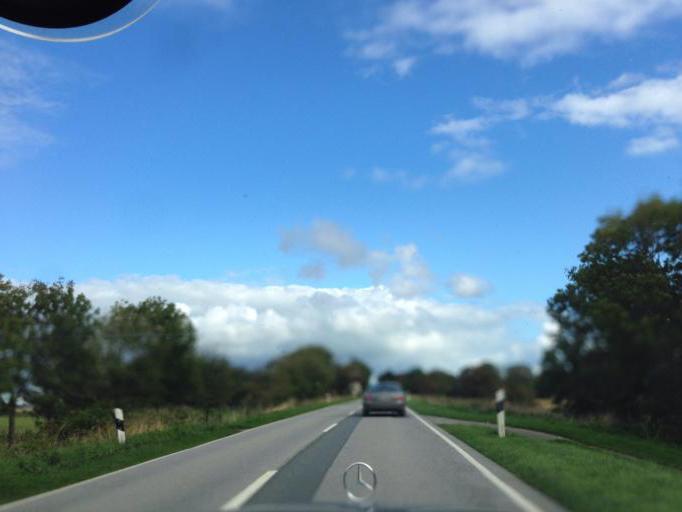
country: DE
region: Schleswig-Holstein
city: Galmsbull
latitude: 54.7746
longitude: 8.7684
